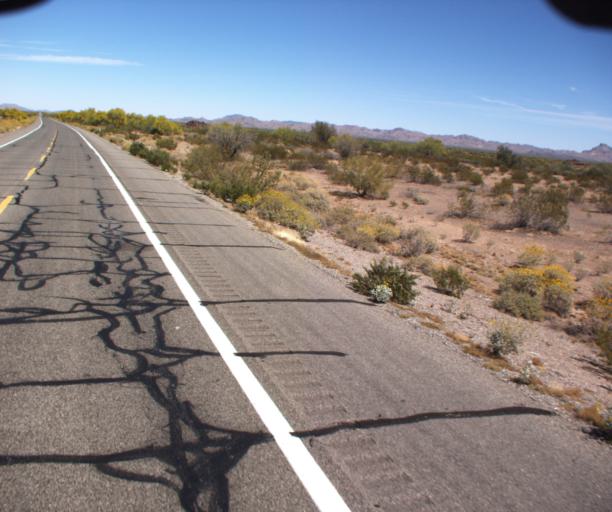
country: US
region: Arizona
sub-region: Pima County
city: Ajo
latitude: 32.5666
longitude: -112.8764
